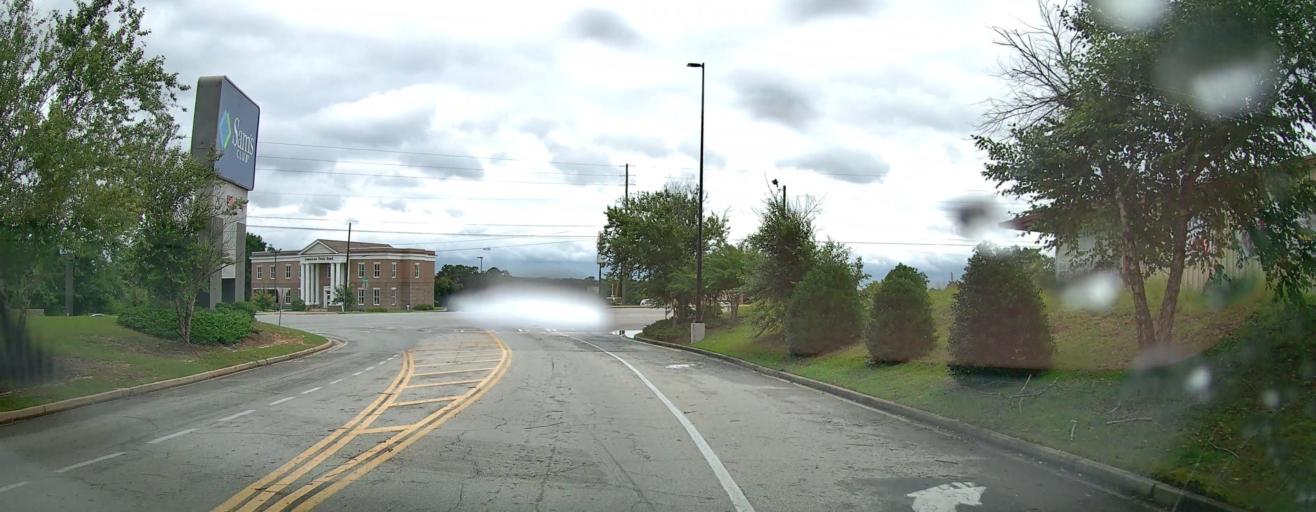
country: US
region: Georgia
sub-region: Bibb County
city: Macon
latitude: 32.8139
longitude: -83.7074
